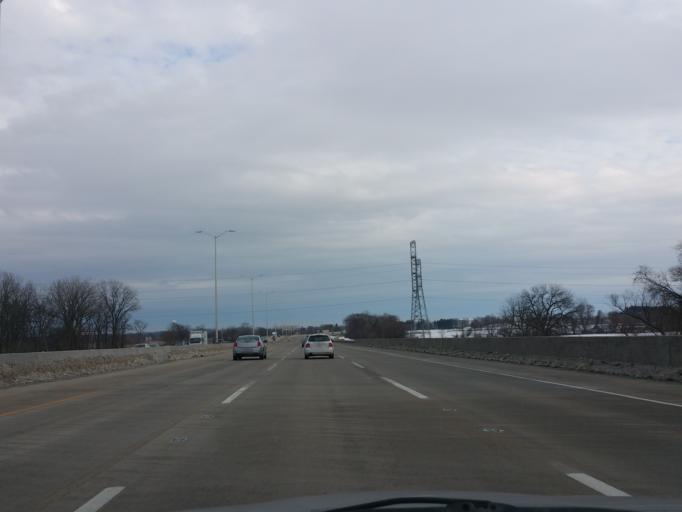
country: US
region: Illinois
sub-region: Winnebago County
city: Cherry Valley
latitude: 42.2471
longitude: -88.9444
